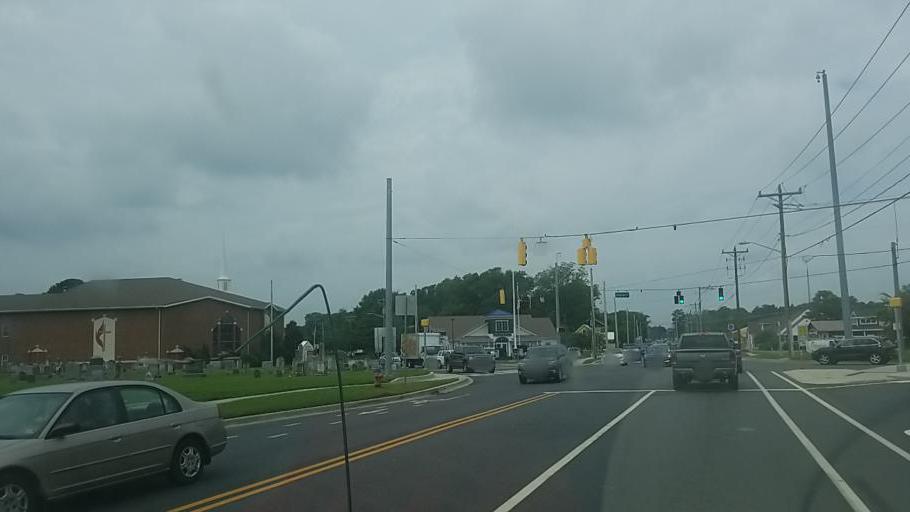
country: US
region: Delaware
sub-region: Sussex County
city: Ocean View
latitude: 38.5443
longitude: -75.0904
